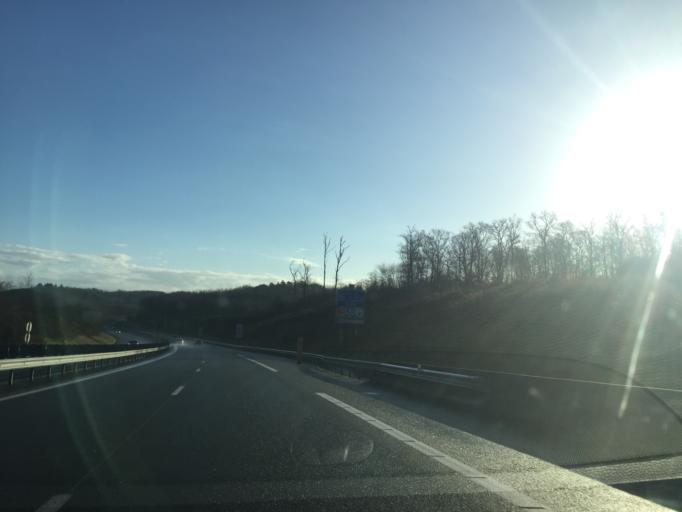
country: FR
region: Limousin
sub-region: Departement de la Correze
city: Saint-Pantaleon-de-Larche
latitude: 45.1617
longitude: 1.4286
